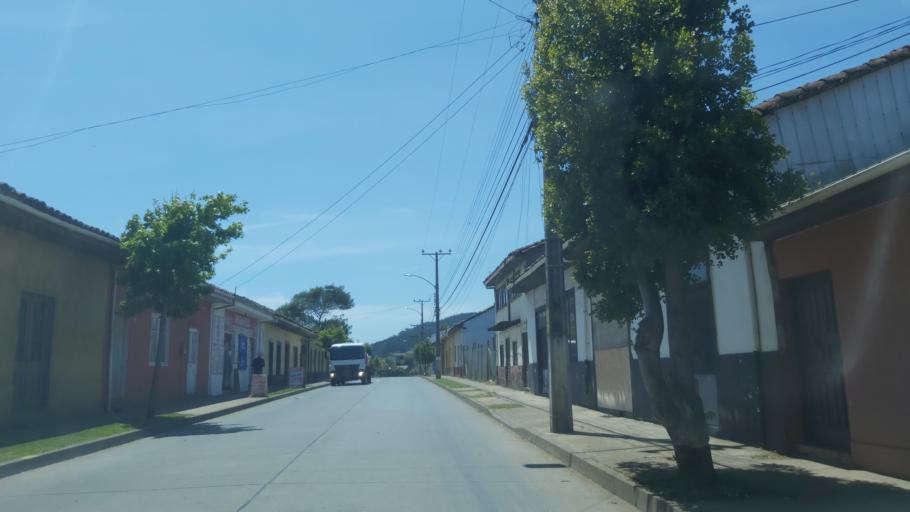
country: CL
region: Maule
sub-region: Provincia de Cauquenes
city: Cauquenes
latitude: -35.8452
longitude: -72.6356
